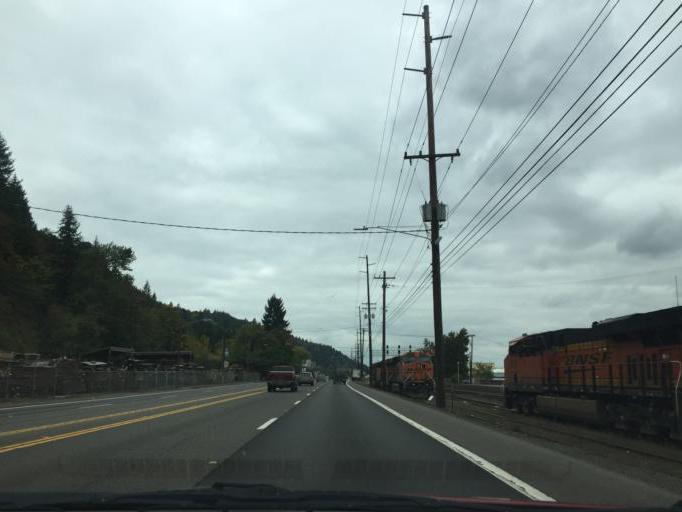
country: US
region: Oregon
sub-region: Washington County
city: West Haven
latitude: 45.5601
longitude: -122.7412
